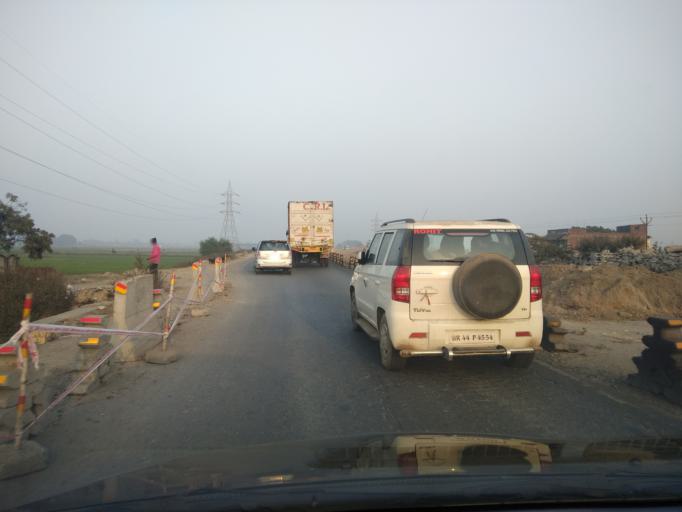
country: IN
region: Uttar Pradesh
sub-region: Chandauli District
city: Mughal Sarai
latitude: 25.2619
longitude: 83.1385
